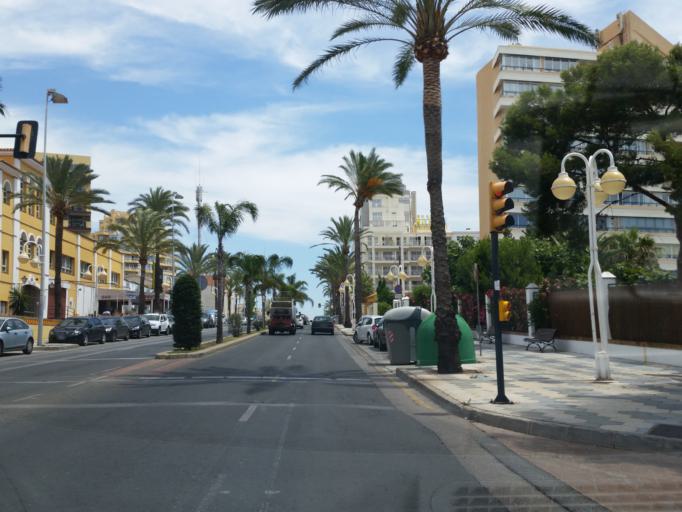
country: ES
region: Andalusia
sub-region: Provincia de Malaga
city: Torremolinos
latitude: 36.5933
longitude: -4.5226
